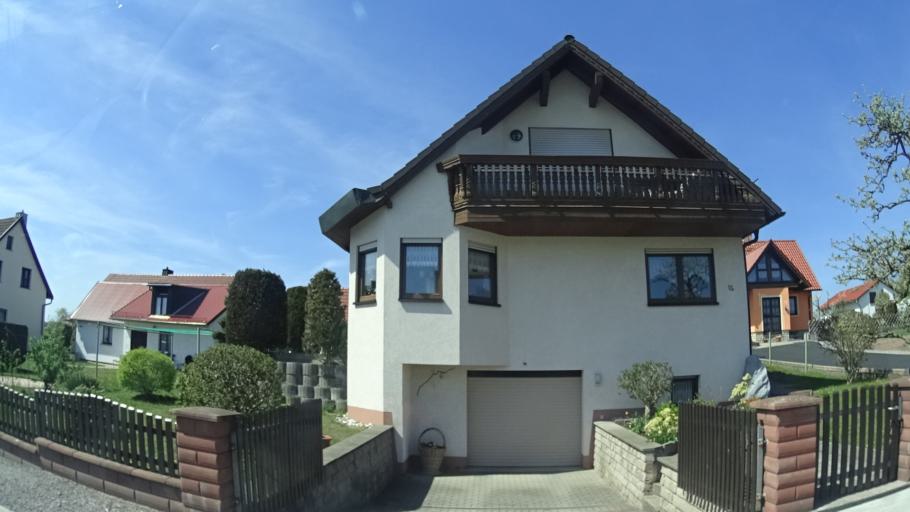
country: DE
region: Thuringia
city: Hildburghausen
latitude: 50.4297
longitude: 10.7421
